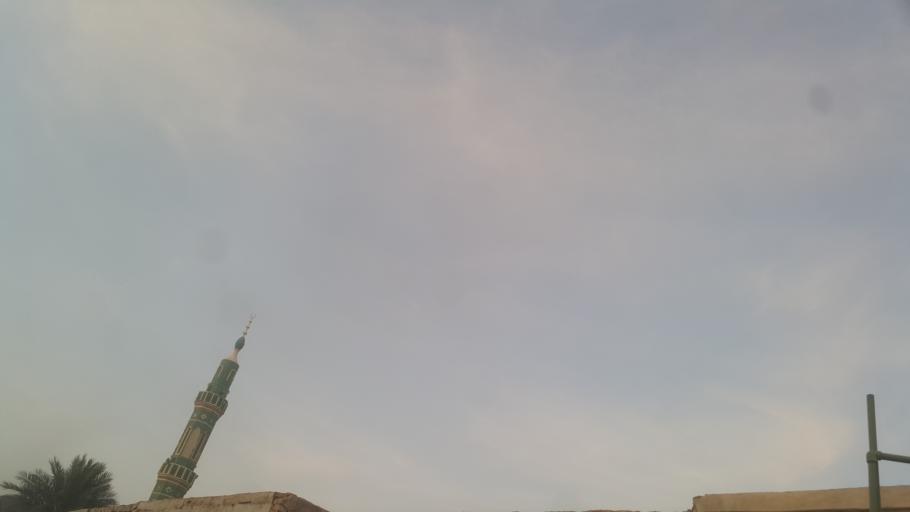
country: SD
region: Khartoum
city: Khartoum
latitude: 15.4486
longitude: 32.4931
